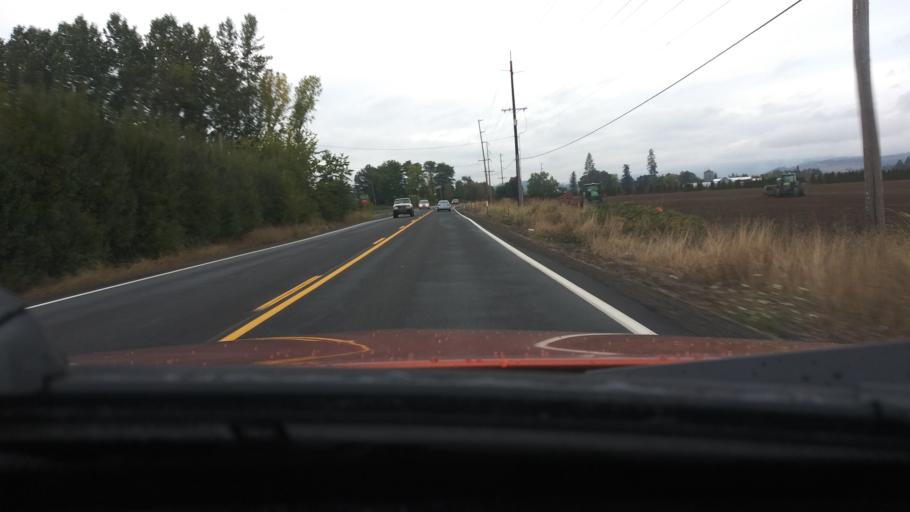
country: US
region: Oregon
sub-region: Washington County
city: Banks
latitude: 45.5804
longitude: -123.1128
